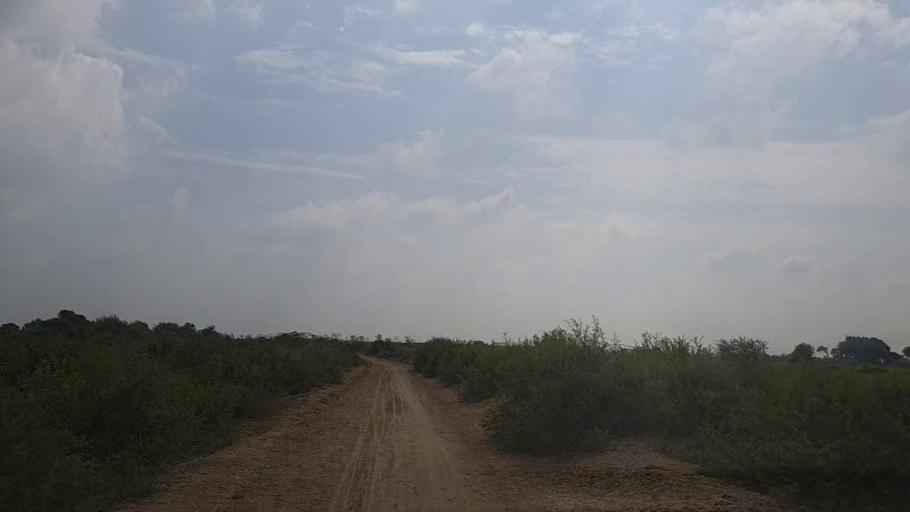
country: PK
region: Sindh
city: Mirpur Batoro
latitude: 24.6079
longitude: 68.1390
